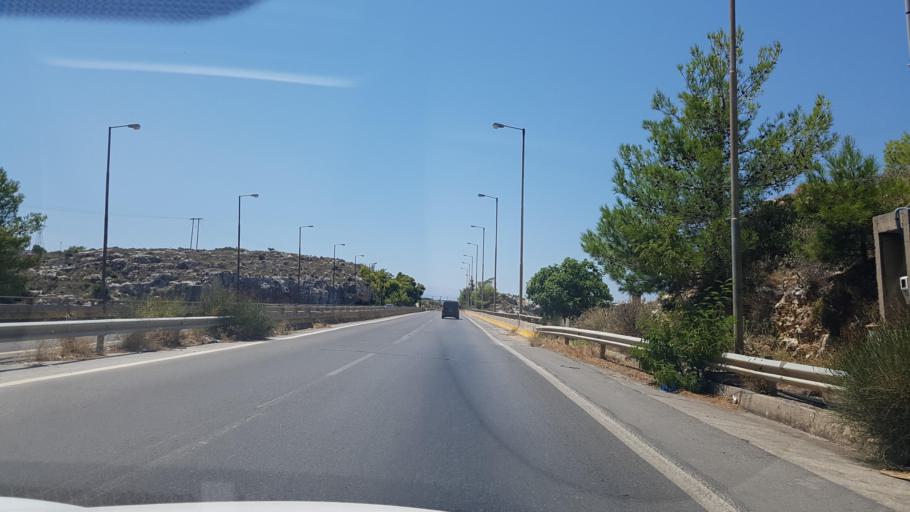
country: GR
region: Crete
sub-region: Nomos Rethymnis
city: Rethymno
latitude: 35.3558
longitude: 24.4780
